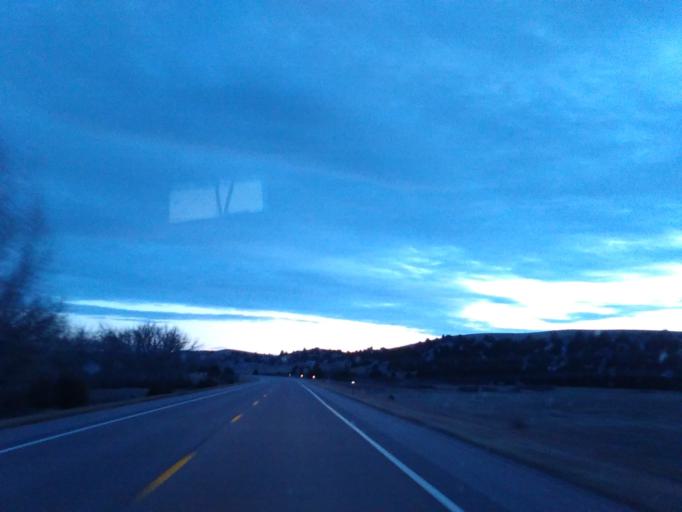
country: US
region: Nebraska
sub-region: Garden County
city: Oshkosh
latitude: 41.2752
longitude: -102.1154
